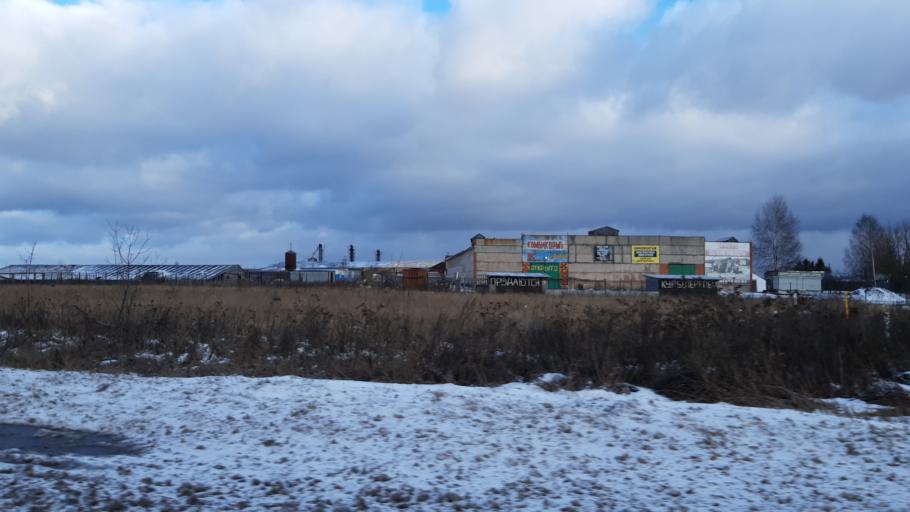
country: RU
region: Moskovskaya
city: Noginsk-9
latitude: 56.0151
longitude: 38.5580
